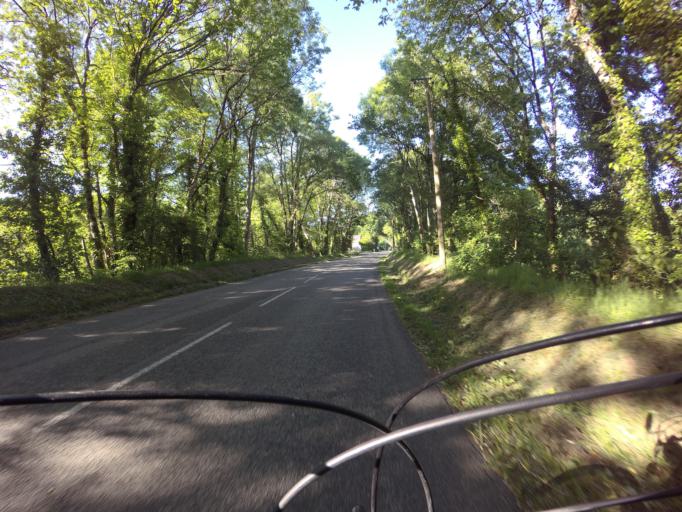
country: FR
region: Brittany
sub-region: Departement du Finistere
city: Quimper
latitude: 48.0183
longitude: -4.1355
